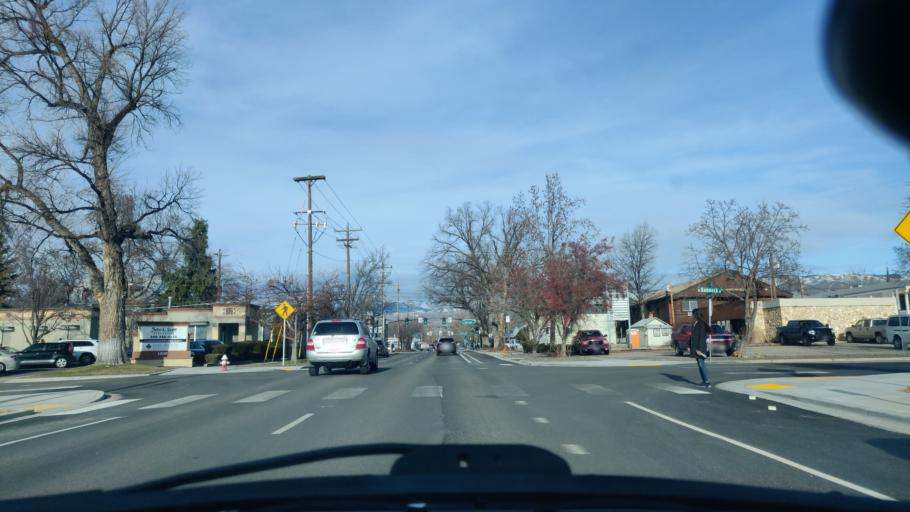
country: US
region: Idaho
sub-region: Ada County
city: Boise
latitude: 43.6211
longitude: -116.2104
